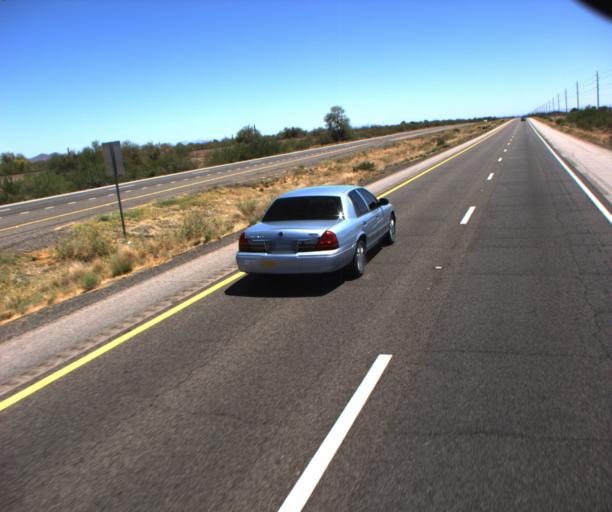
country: US
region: Arizona
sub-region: Maricopa County
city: Wickenburg
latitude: 33.7960
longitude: -112.5521
